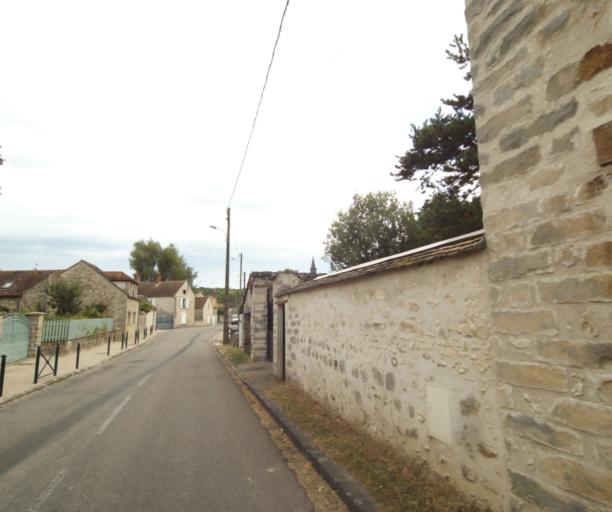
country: FR
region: Ile-de-France
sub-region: Departement de Seine-et-Marne
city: Cely
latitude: 48.4573
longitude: 2.5375
